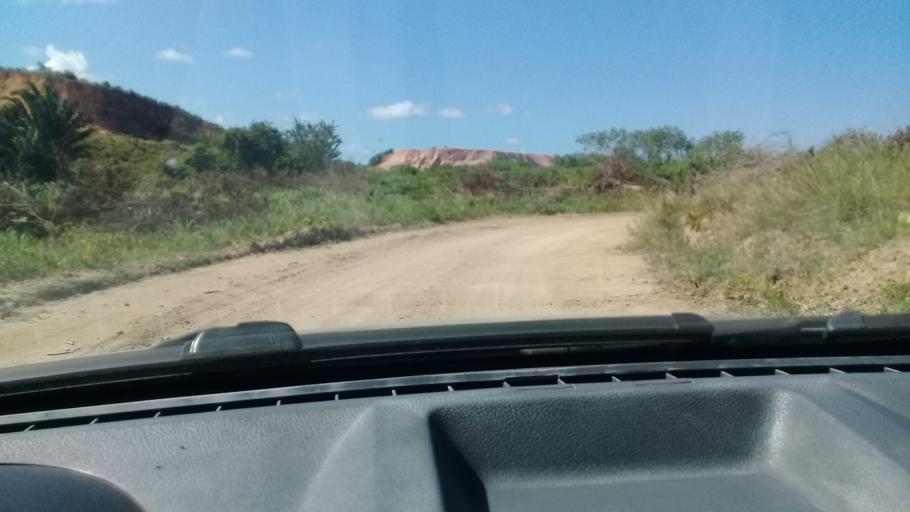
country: BR
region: Pernambuco
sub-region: Jaboatao Dos Guararapes
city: Jaboatao
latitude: -8.1498
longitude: -34.9518
